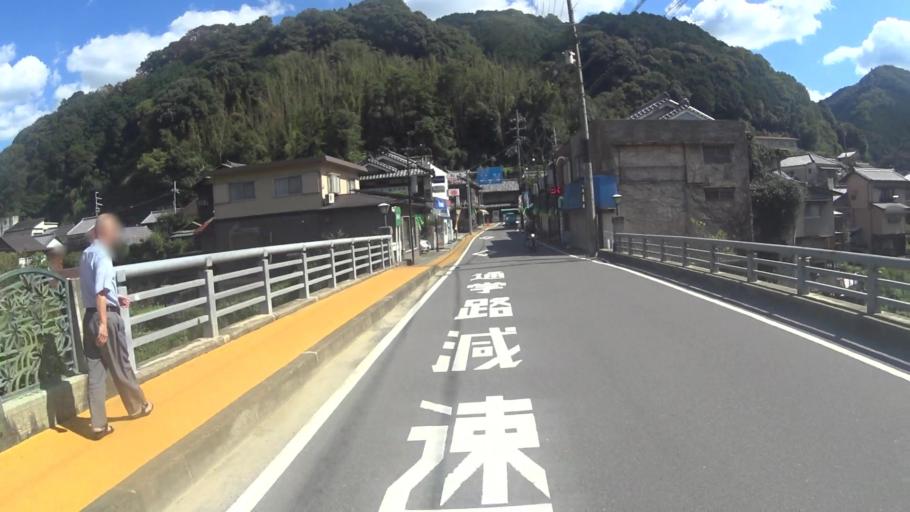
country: JP
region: Nara
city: Nara-shi
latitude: 34.7579
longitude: 135.9358
